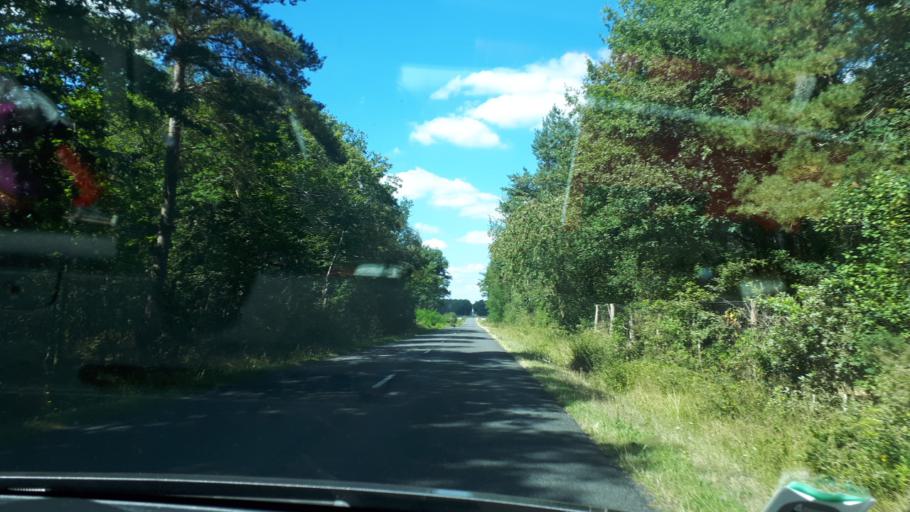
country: FR
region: Centre
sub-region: Departement du Loir-et-Cher
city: Neung-sur-Beuvron
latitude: 47.5341
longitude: 1.7378
